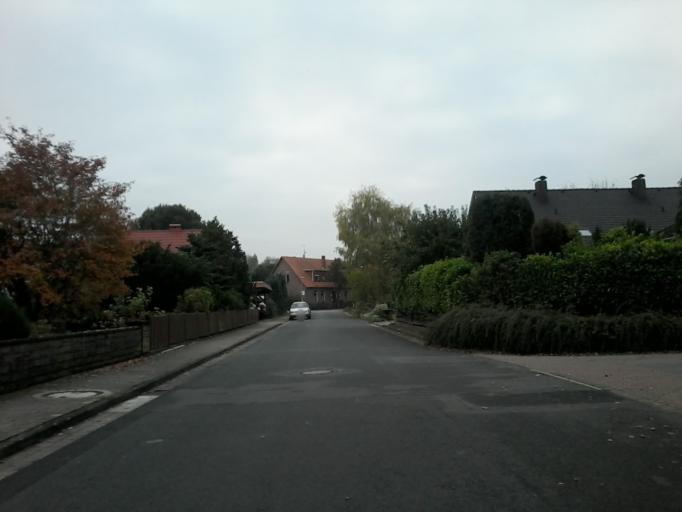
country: DE
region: Lower Saxony
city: Ahsen-Oetzen
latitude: 53.0030
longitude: 9.0859
